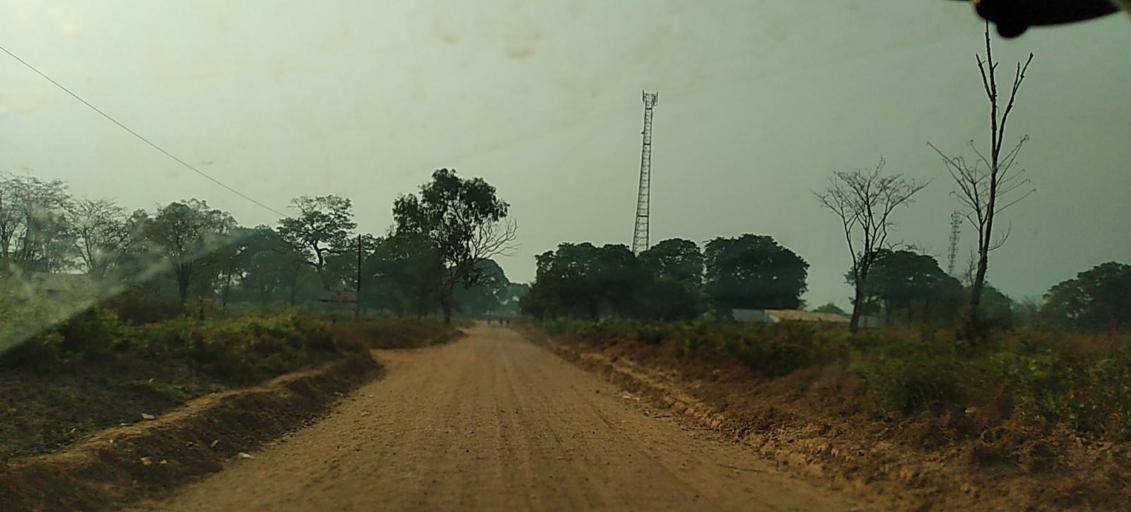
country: ZM
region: North-Western
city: Kabompo
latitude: -13.5970
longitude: 24.2054
